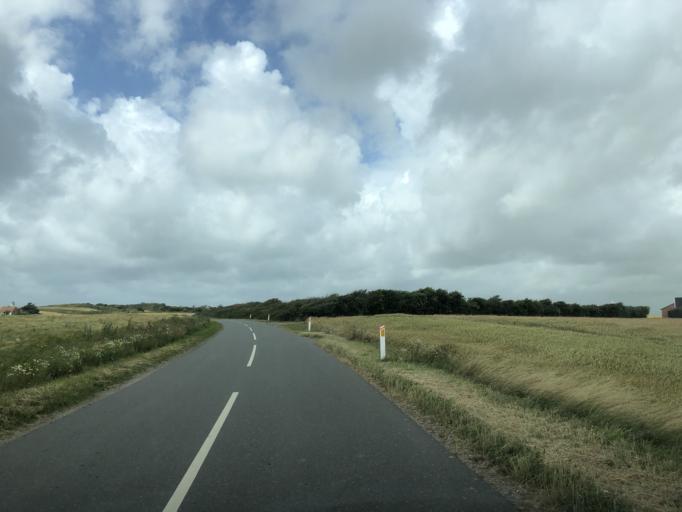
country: DK
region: Central Jutland
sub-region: Lemvig Kommune
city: Harboore
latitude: 56.4886
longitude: 8.1383
